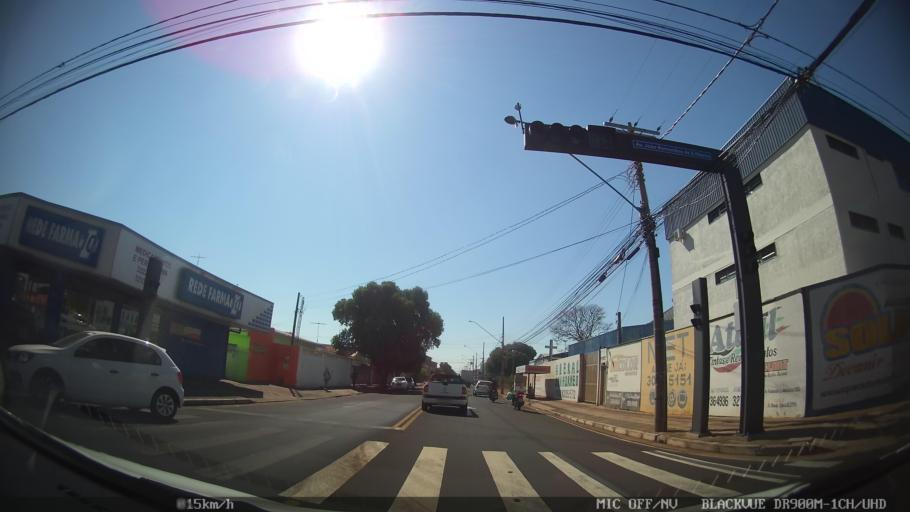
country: BR
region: Sao Paulo
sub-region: Sao Jose Do Rio Preto
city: Sao Jose do Rio Preto
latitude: -20.8061
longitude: -49.4023
